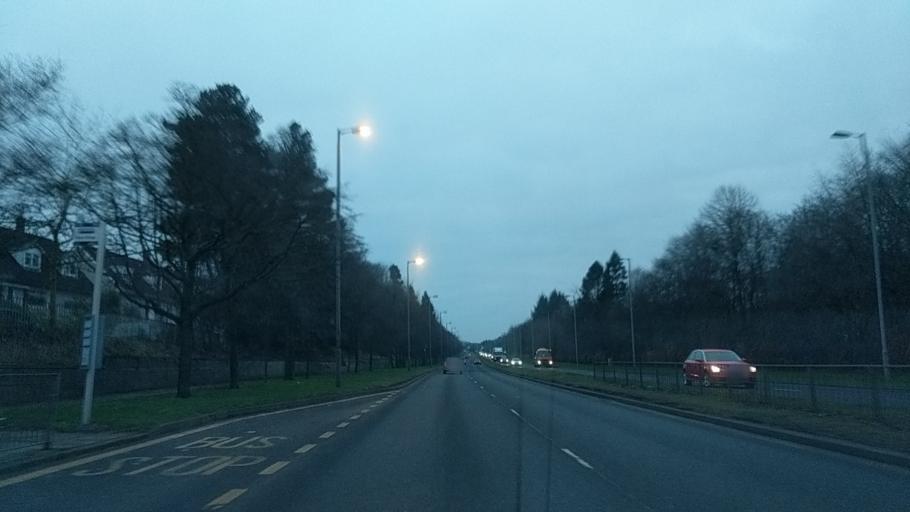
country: GB
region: Scotland
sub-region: South Lanarkshire
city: East Kilbride
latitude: 55.7725
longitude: -4.1637
